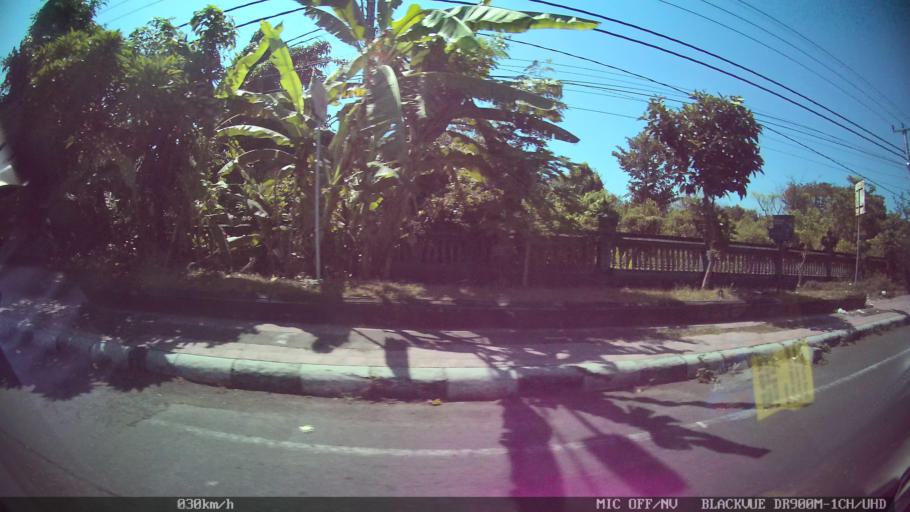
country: ID
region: Bali
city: Banjar Banyualit
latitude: -8.1552
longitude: 115.0363
